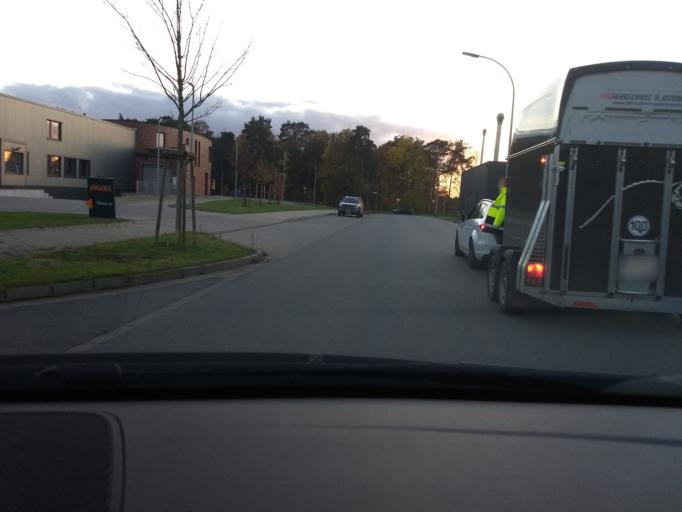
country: DE
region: North Rhine-Westphalia
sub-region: Regierungsbezirk Munster
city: Borken
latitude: 51.8510
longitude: 6.8907
